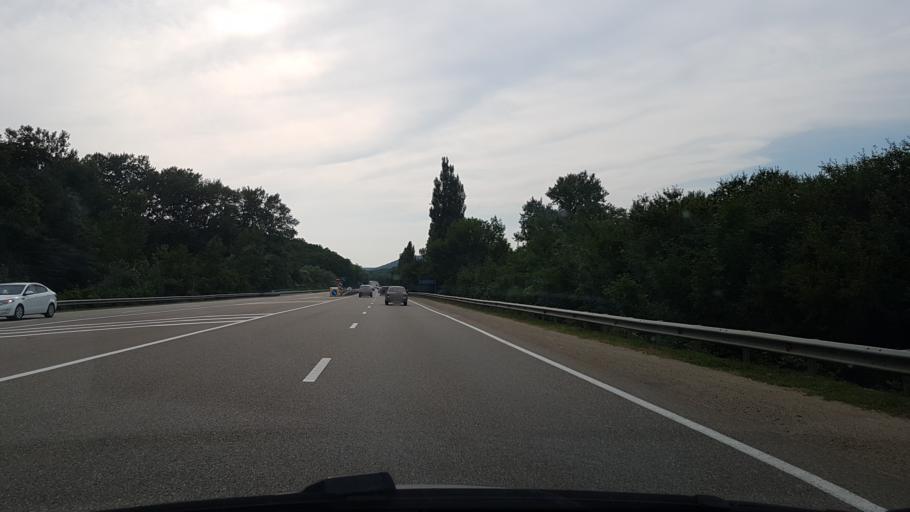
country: RU
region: Krasnodarskiy
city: Goryachiy Klyuch
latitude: 44.5987
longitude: 39.0460
